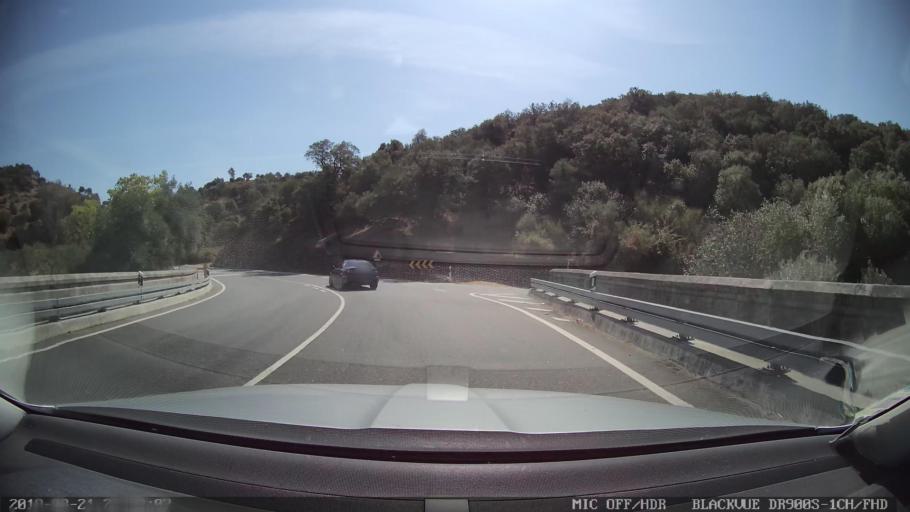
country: PT
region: Castelo Branco
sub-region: Idanha-A-Nova
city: Idanha-a-Nova
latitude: 39.8584
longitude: -7.3330
